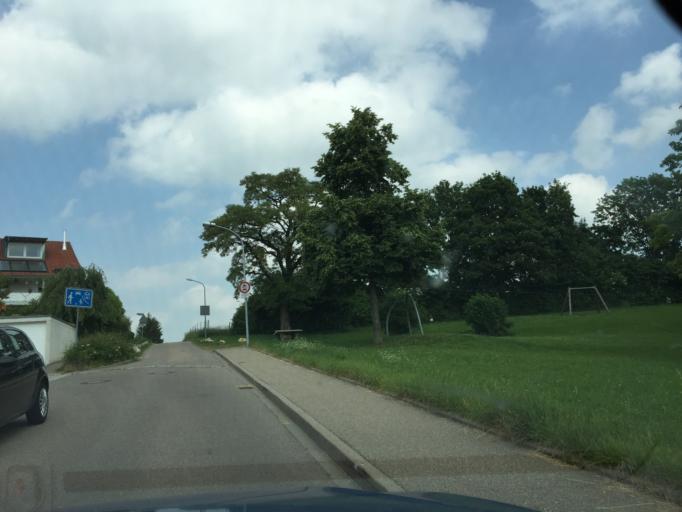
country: DE
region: Bavaria
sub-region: Swabia
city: Senden
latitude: 48.3295
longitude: 10.0622
